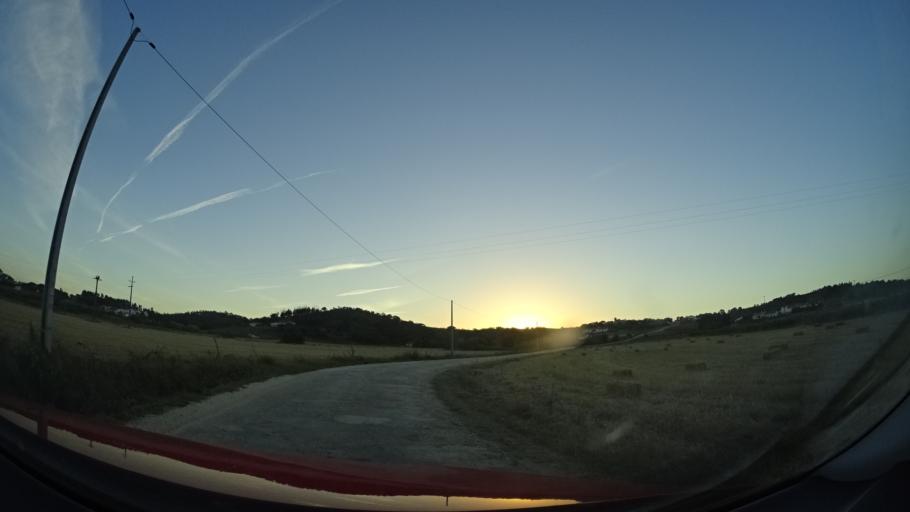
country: PT
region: Faro
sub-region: Aljezur
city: Aljezur
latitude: 37.2376
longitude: -8.8277
